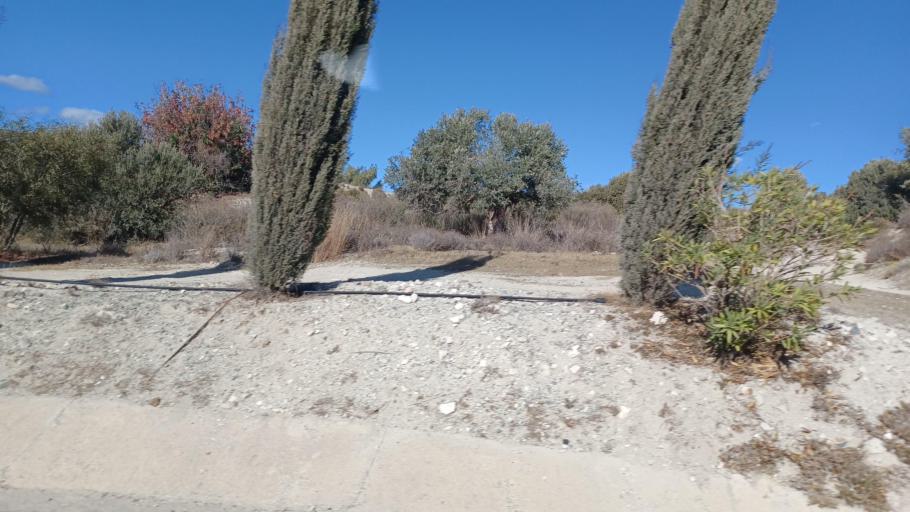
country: CY
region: Limassol
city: Pyrgos
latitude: 34.7650
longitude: 33.2310
